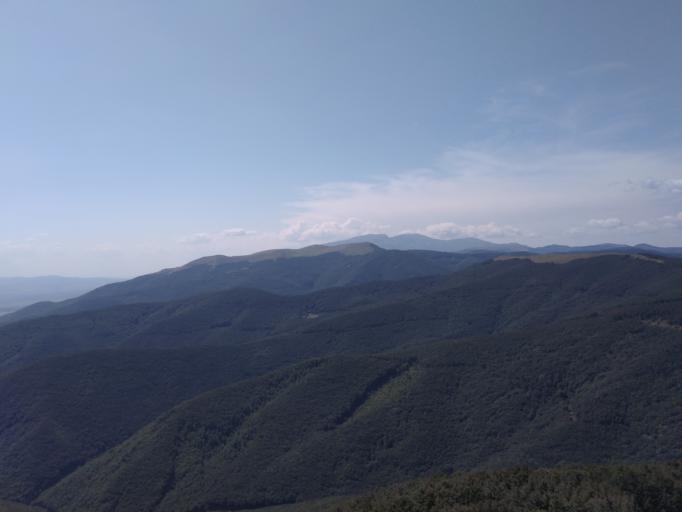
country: BG
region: Stara Zagora
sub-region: Obshtina Kazanluk
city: Shipka
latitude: 42.7481
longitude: 25.3215
